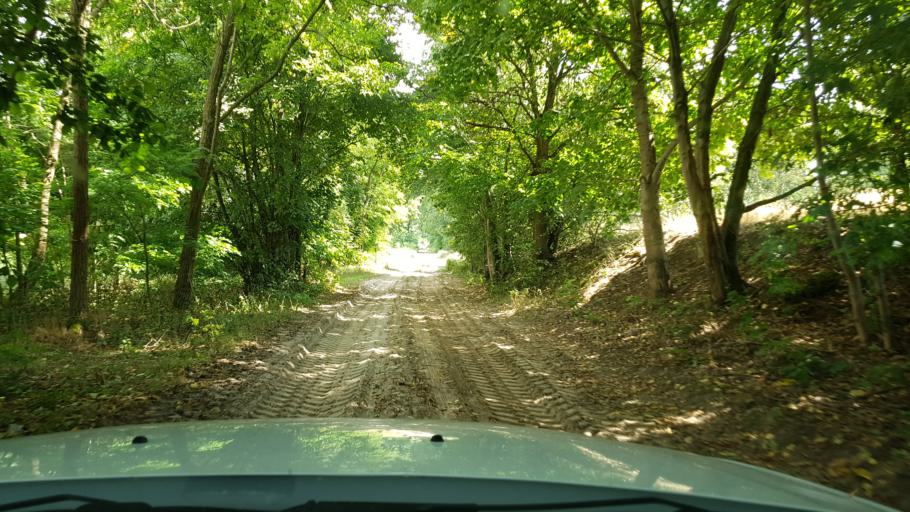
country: PL
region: West Pomeranian Voivodeship
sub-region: Powiat walecki
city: Walcz
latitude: 53.2529
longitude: 16.5099
